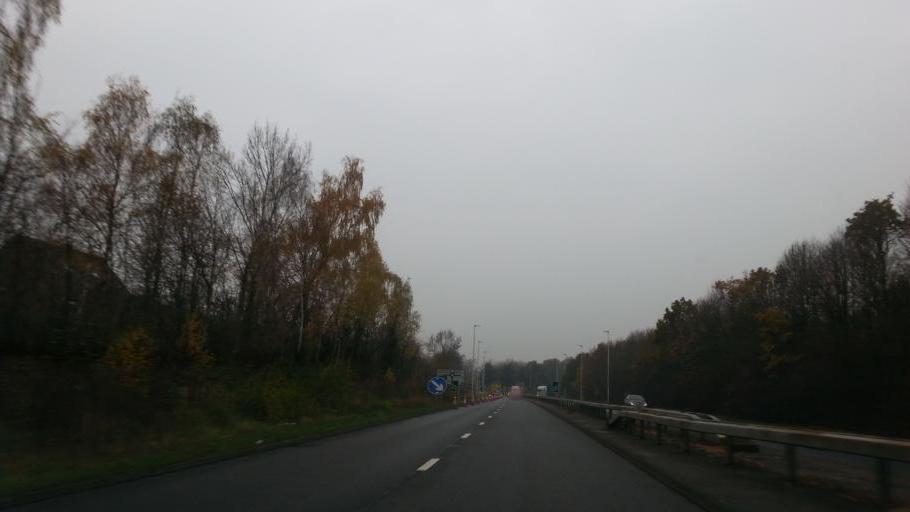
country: GB
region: England
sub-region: Peterborough
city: Castor
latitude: 52.5497
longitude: -0.3102
